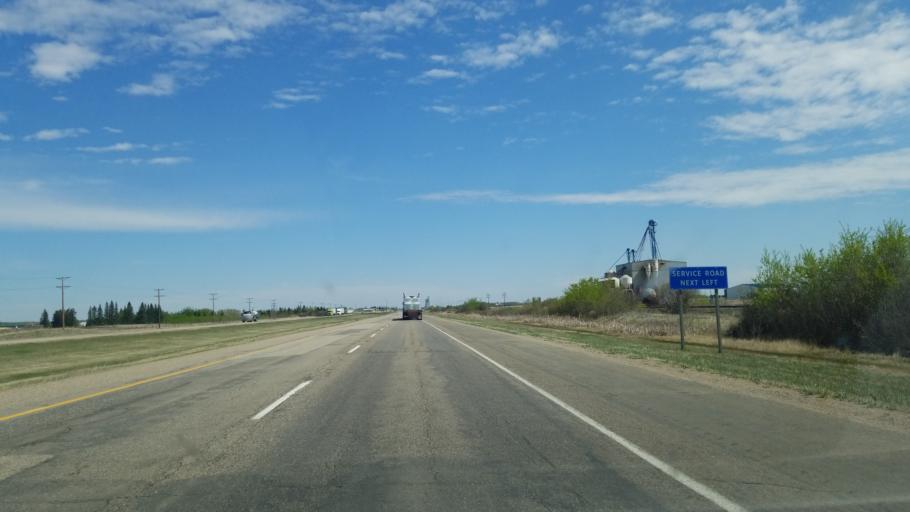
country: CA
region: Saskatchewan
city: Lloydminster
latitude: 53.1366
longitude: -109.6472
